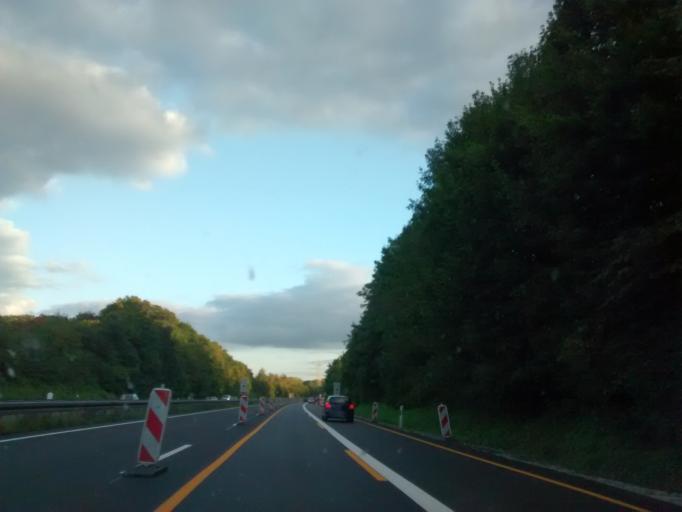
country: DE
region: Lower Saxony
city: Osnabrueck
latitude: 52.2599
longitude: 8.0101
